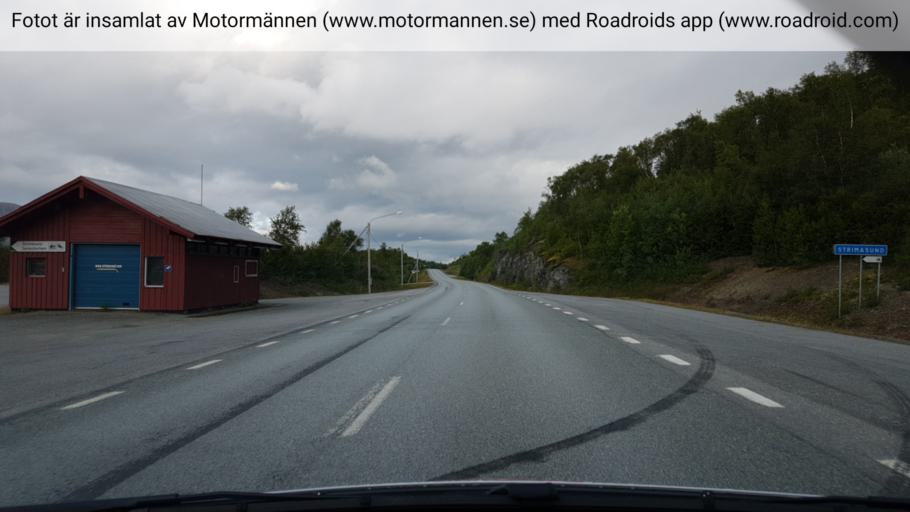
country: NO
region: Nordland
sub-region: Rana
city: Mo i Rana
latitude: 66.0534
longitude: 14.8831
